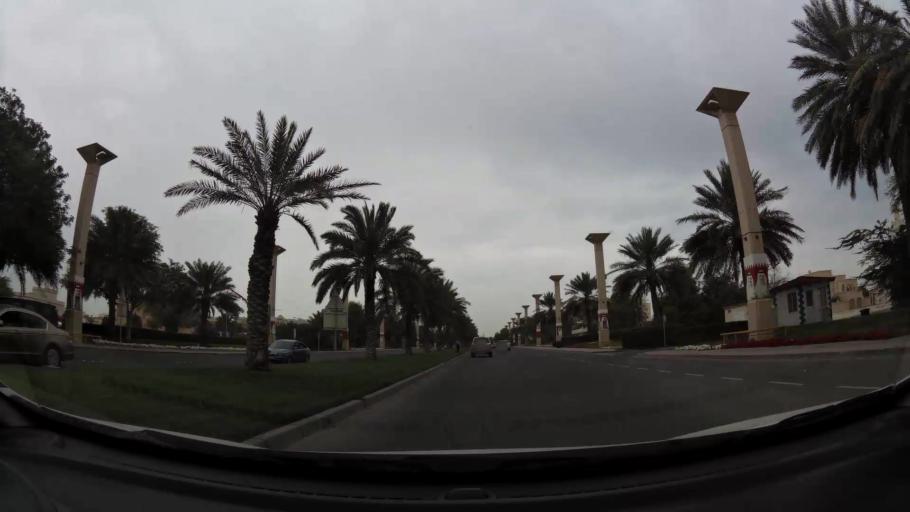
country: BH
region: Northern
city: Ar Rifa'
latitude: 26.1315
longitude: 50.5376
